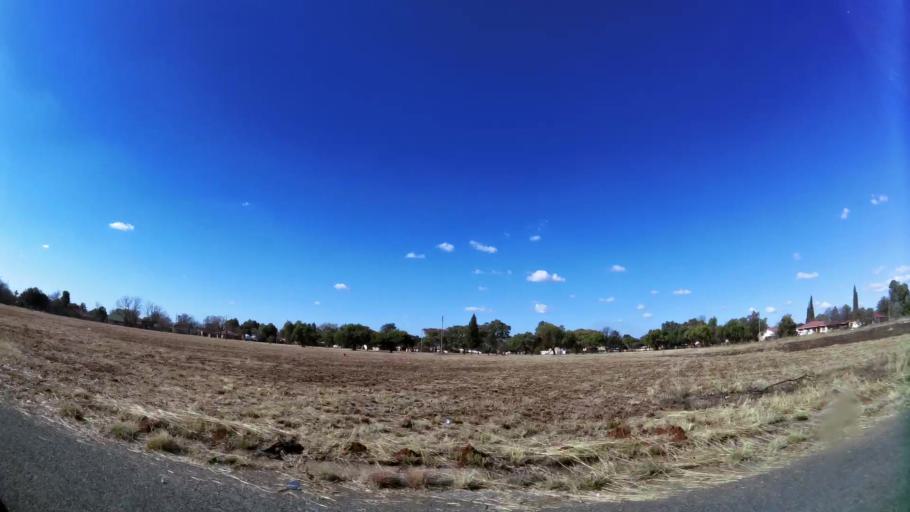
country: ZA
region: Gauteng
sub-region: West Rand District Municipality
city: Carletonville
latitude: -26.3670
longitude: 27.3776
